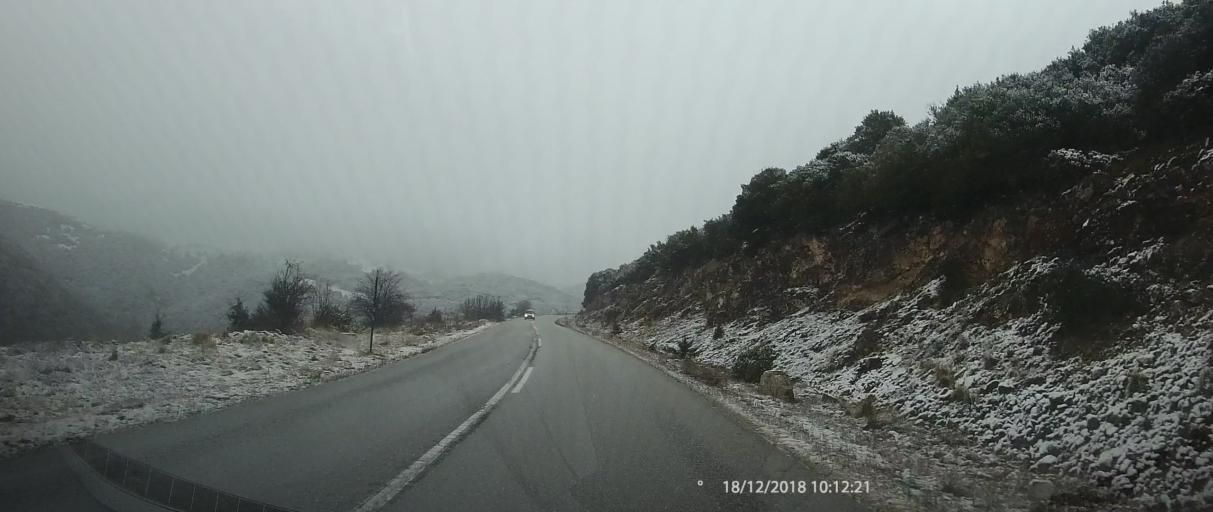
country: GR
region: Thessaly
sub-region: Nomos Larisis
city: Livadi
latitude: 40.0976
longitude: 22.2061
